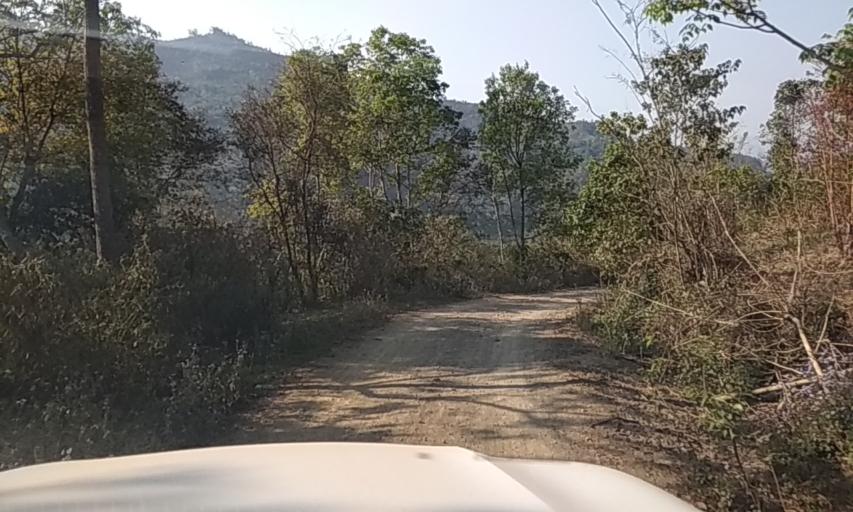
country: LA
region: Phongsali
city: Phongsali
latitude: 21.6937
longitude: 102.0929
